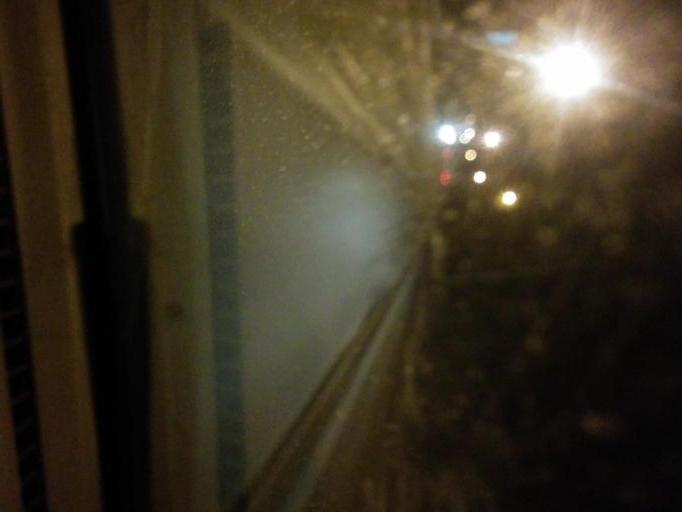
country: US
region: Pennsylvania
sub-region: Allegheny County
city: Aspinwall
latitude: 40.4789
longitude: -79.9079
